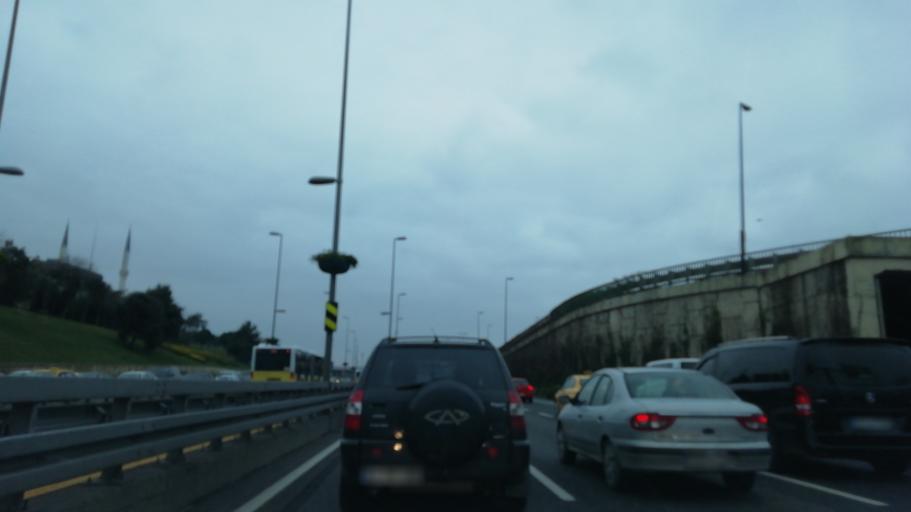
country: TR
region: Istanbul
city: UEskuedar
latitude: 41.0268
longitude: 29.0460
